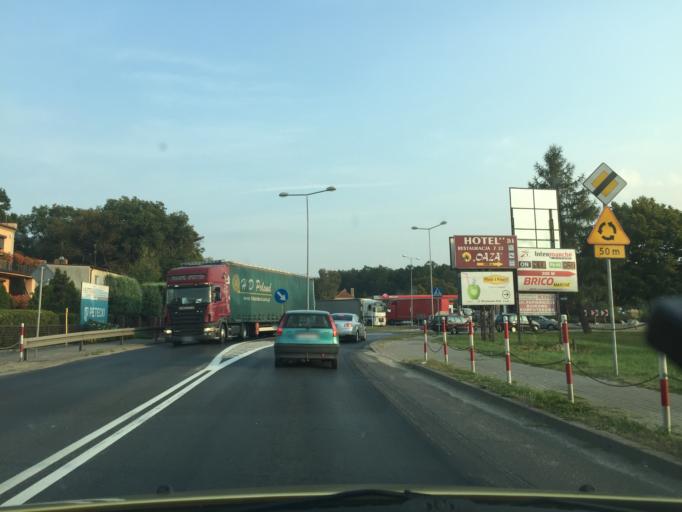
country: PL
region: Greater Poland Voivodeship
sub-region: Powiat jarocinski
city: Jarocin
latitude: 51.9569
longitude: 17.5181
